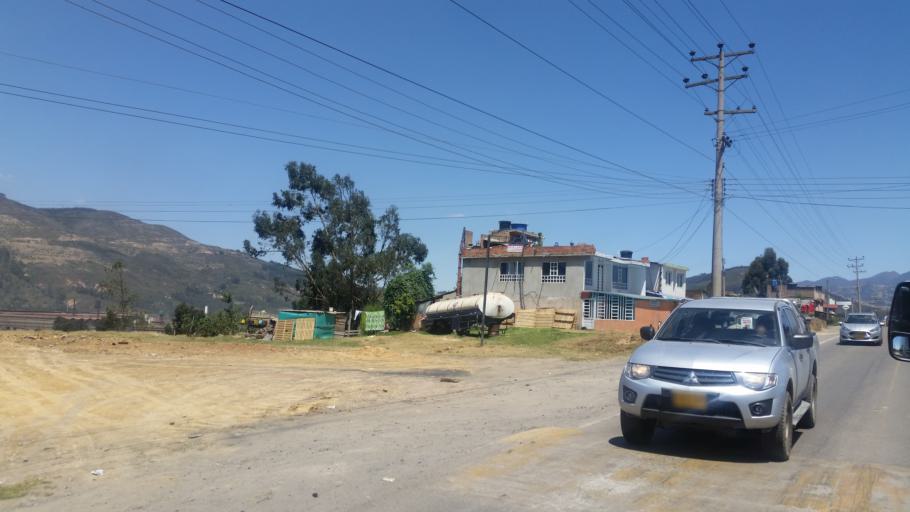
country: CO
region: Boyaca
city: Mongui
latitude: 5.7611
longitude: -72.8852
